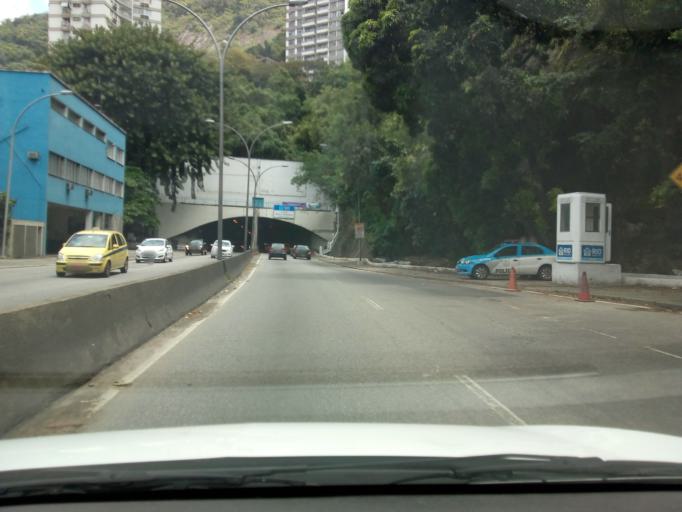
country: BR
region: Rio de Janeiro
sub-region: Rio De Janeiro
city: Rio de Janeiro
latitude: -22.9311
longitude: -43.1856
